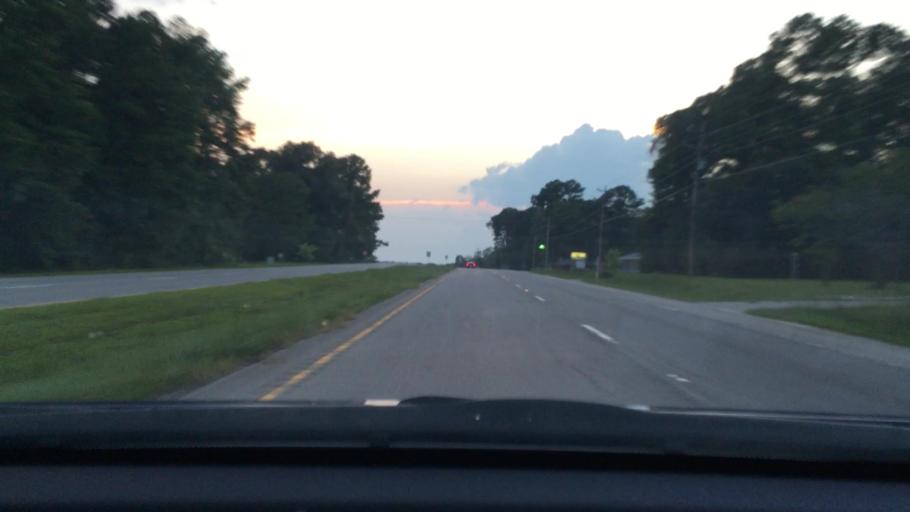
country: US
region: South Carolina
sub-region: Richland County
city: Gadsden
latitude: 33.9436
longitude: -80.7379
